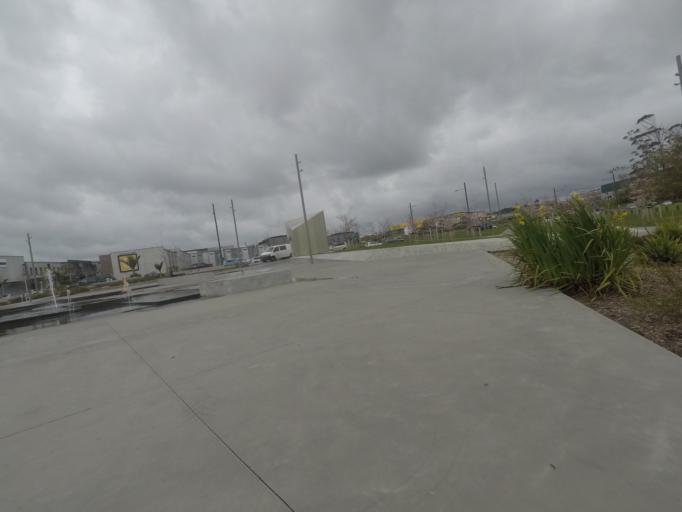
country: NZ
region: Auckland
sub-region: Auckland
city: Rosebank
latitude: -36.8165
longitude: 174.6089
